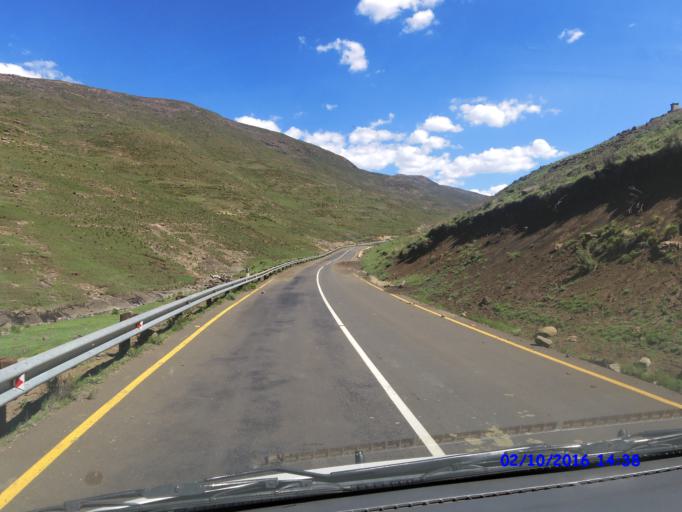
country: LS
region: Maseru
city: Nako
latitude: -29.5072
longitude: 28.0631
